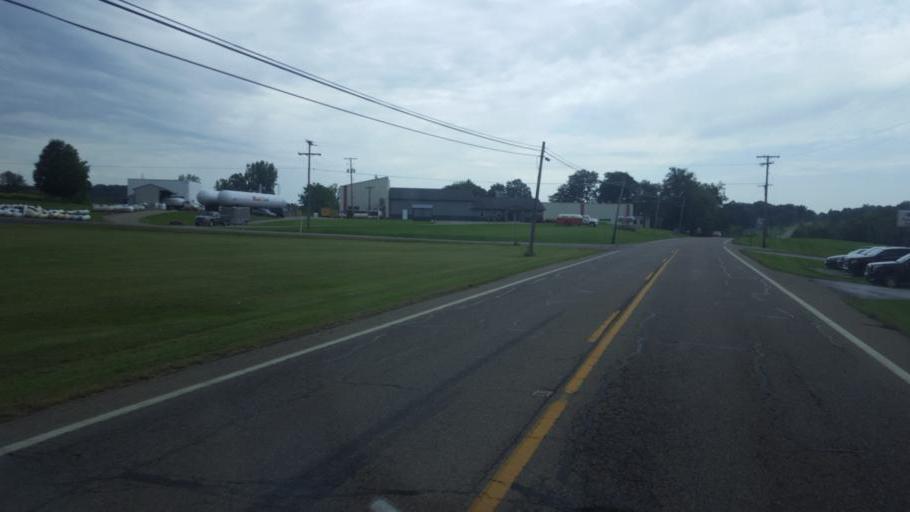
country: US
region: Ohio
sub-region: Knox County
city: Mount Vernon
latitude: 40.4297
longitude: -82.4511
